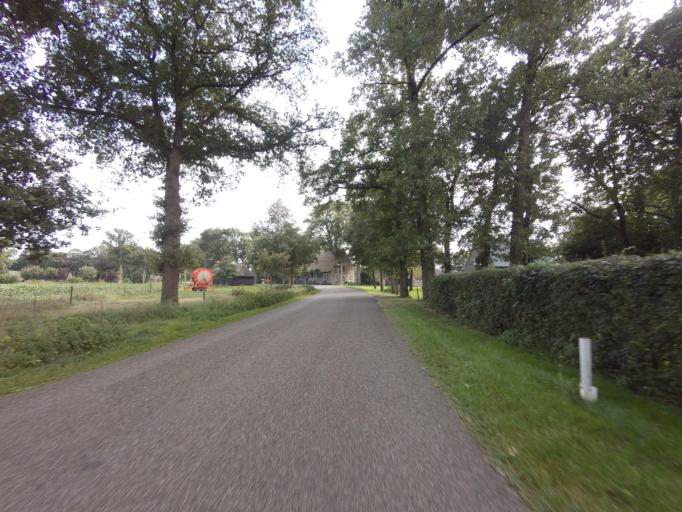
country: DE
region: Lower Saxony
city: Wielen
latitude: 52.5626
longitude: 6.6698
